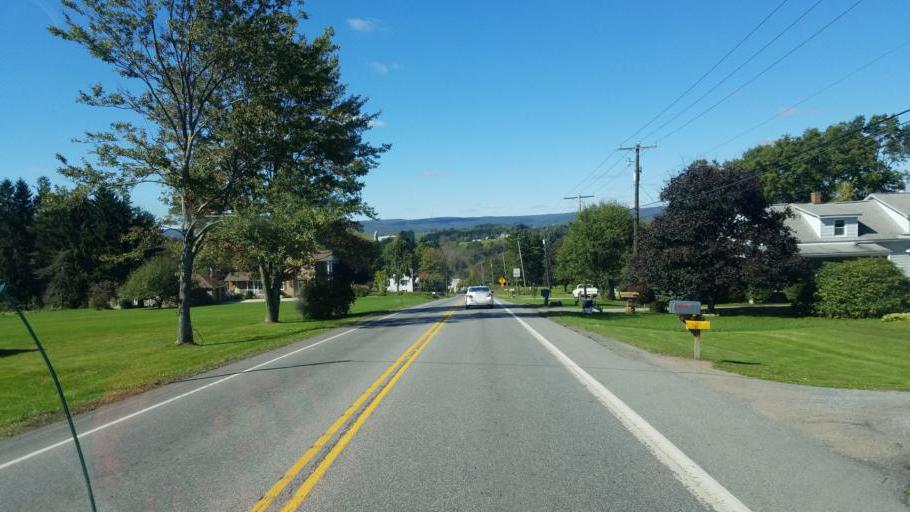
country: US
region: Pennsylvania
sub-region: Somerset County
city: Boswell
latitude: 40.1445
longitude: -79.0341
